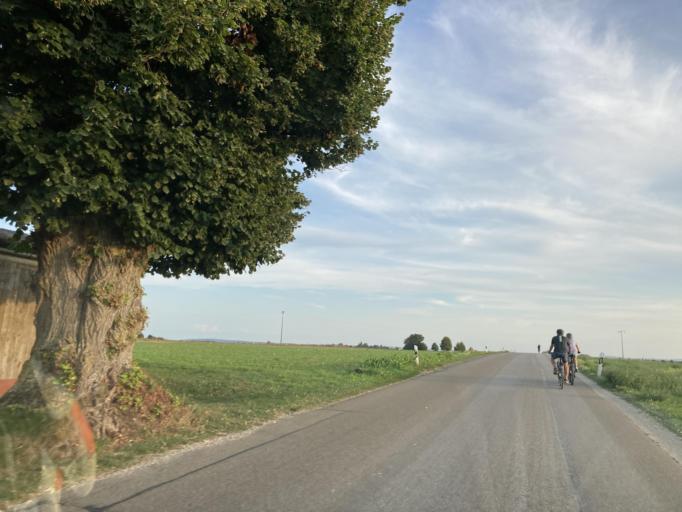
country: DE
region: Bavaria
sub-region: Swabia
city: Munningen
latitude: 48.9270
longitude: 10.6187
